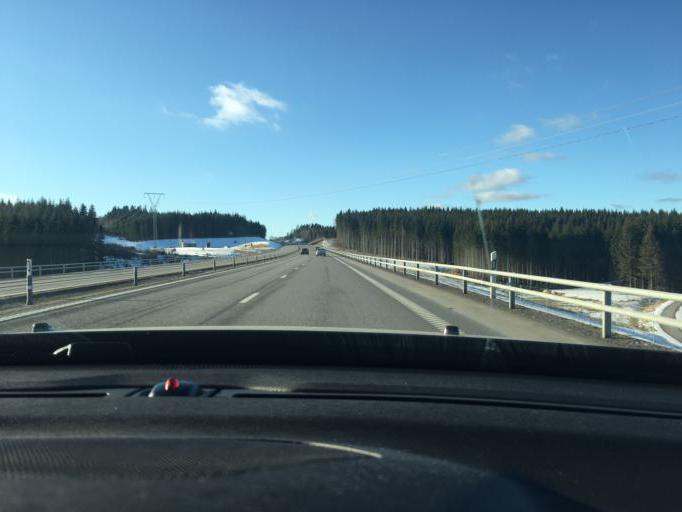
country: SE
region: Vaestra Goetaland
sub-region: Ulricehamns Kommun
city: Ulricehamn
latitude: 57.8164
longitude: 13.3503
